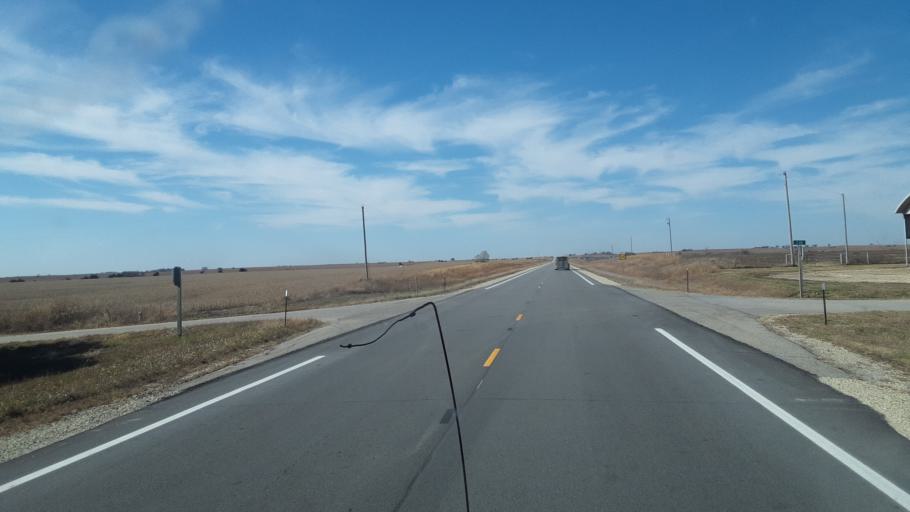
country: US
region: Kansas
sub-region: Marion County
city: Marion
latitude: 38.3628
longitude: -96.8006
